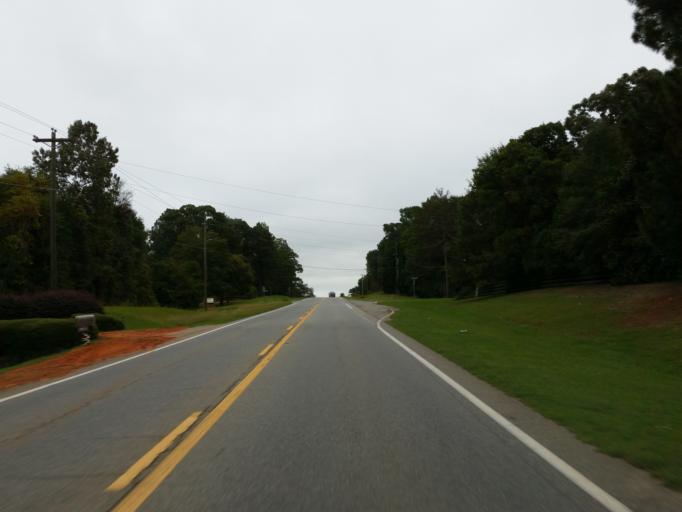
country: US
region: Georgia
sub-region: Houston County
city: Perry
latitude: 32.4853
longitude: -83.7944
